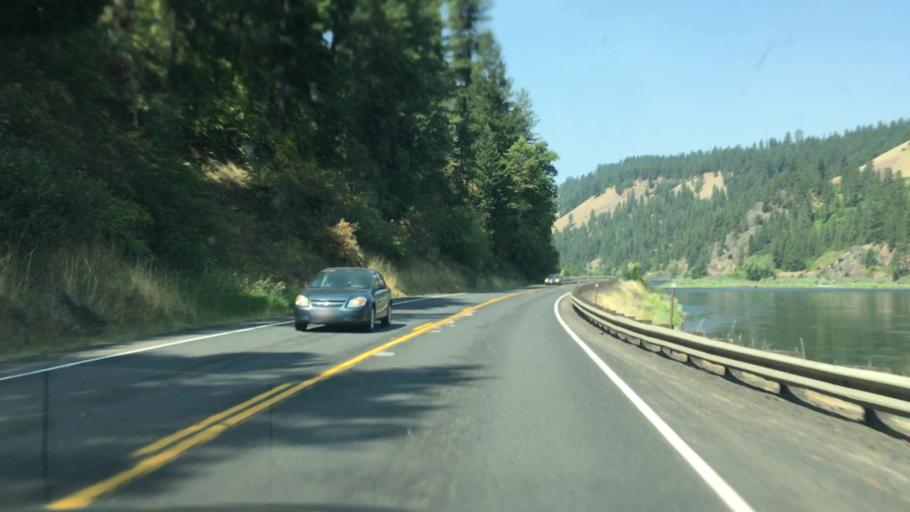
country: US
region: Idaho
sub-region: Clearwater County
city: Orofino
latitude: 46.4985
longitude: -116.3779
